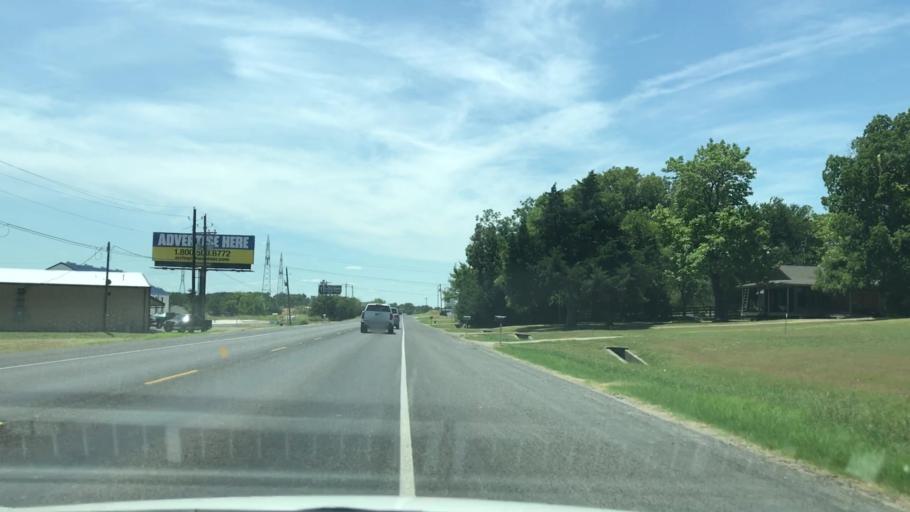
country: US
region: Texas
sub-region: Collin County
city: Lavon
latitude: 33.0083
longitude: -96.4600
